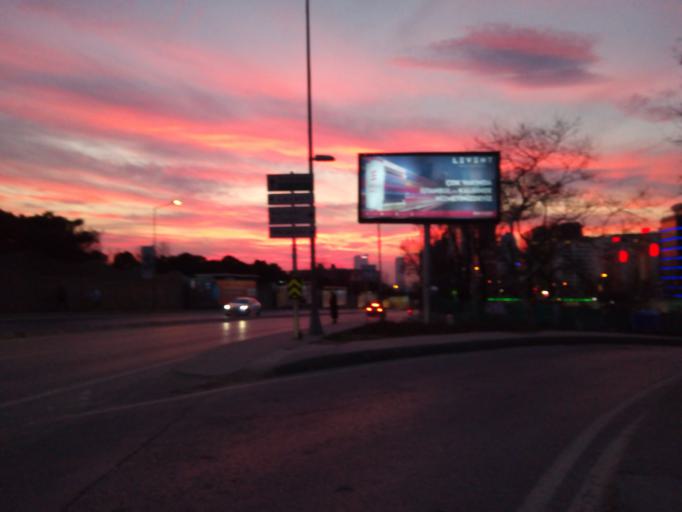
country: TR
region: Istanbul
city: Sisli
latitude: 41.1084
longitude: 29.0251
